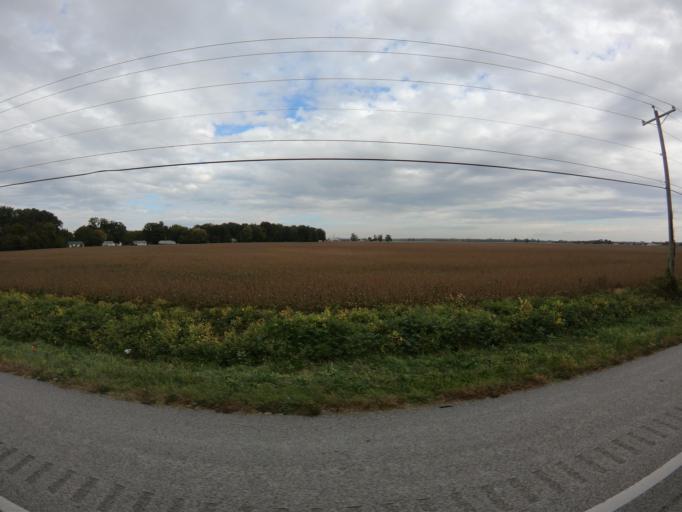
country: US
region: Maryland
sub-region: Queen Anne's County
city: Centreville
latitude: 38.9581
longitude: -76.0925
